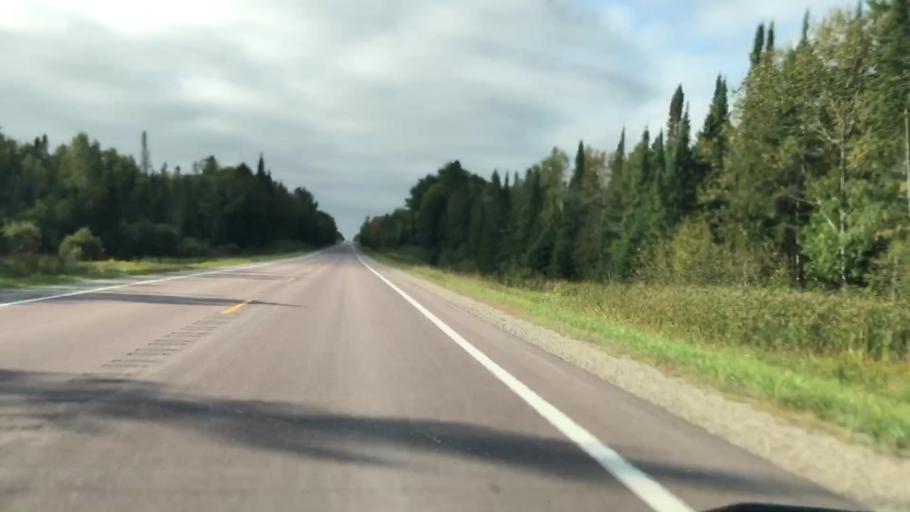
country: US
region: Michigan
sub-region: Luce County
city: Newberry
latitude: 46.2961
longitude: -85.5690
